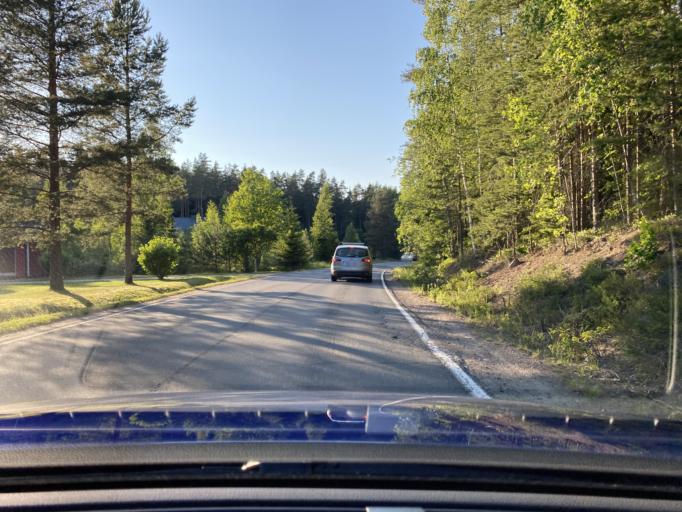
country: FI
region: Haeme
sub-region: Riihimaeki
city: Riihimaeki
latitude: 60.7216
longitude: 24.7046
